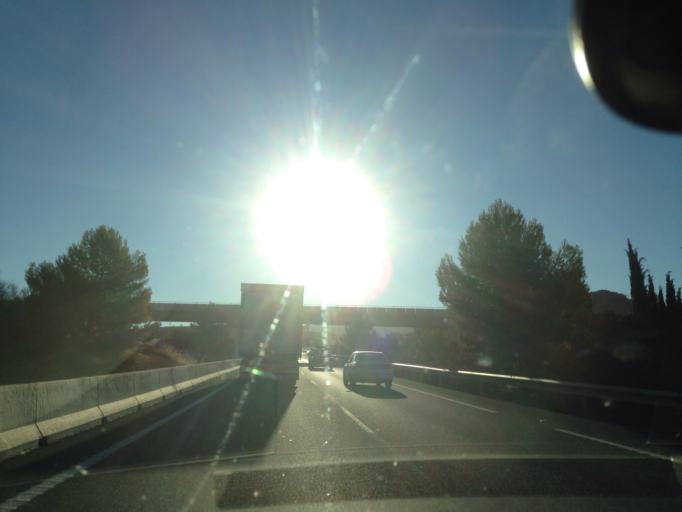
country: ES
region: Andalusia
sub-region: Provincia de Malaga
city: Casabermeja
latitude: 36.9035
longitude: -4.4426
